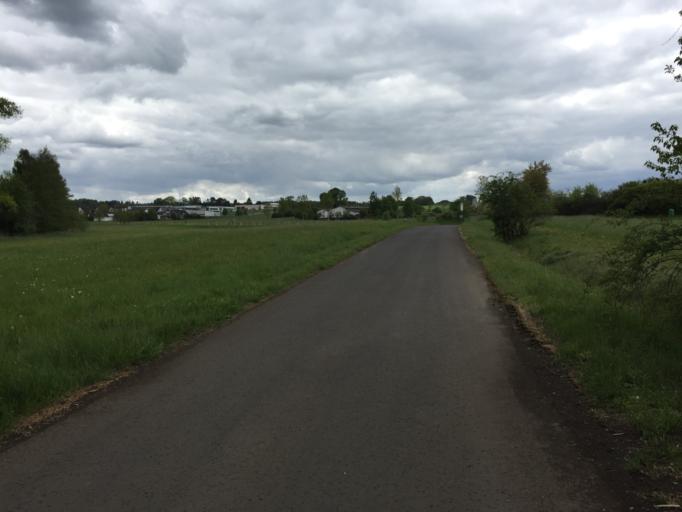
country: DE
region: Hesse
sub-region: Regierungsbezirk Giessen
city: Grunberg
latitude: 50.5666
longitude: 8.8984
